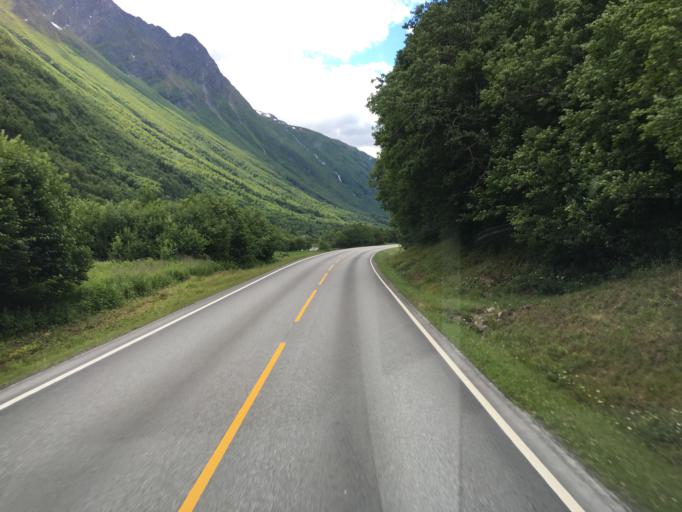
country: NO
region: More og Romsdal
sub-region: Sunndal
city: Sunndalsora
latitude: 62.6256
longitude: 8.8778
